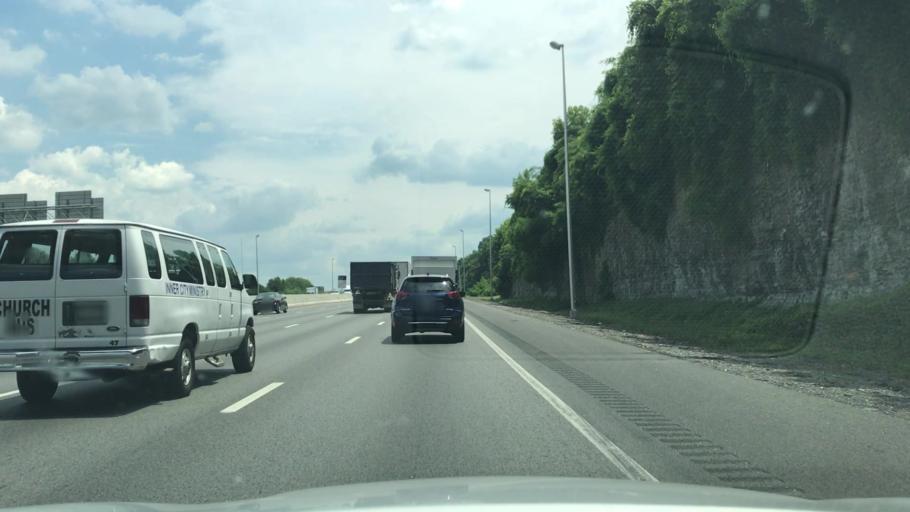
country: US
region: Tennessee
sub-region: Davidson County
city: Oak Hill
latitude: 36.0963
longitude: -86.7085
